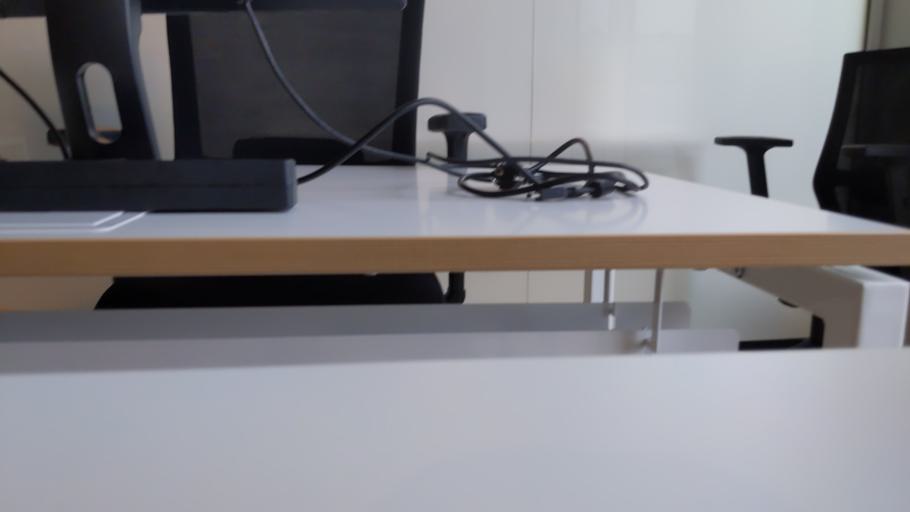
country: RU
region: Moskovskaya
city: Rogachevo
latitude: 56.4263
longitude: 37.1027
